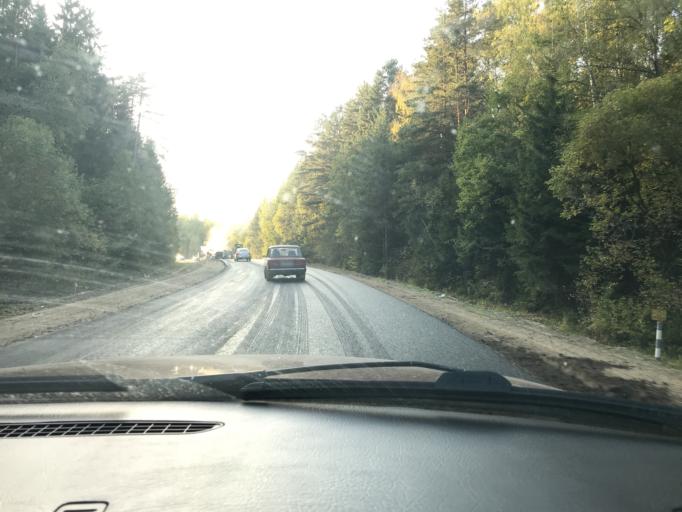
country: RU
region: Kaluga
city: Kondrovo
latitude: 54.7748
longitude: 35.8530
